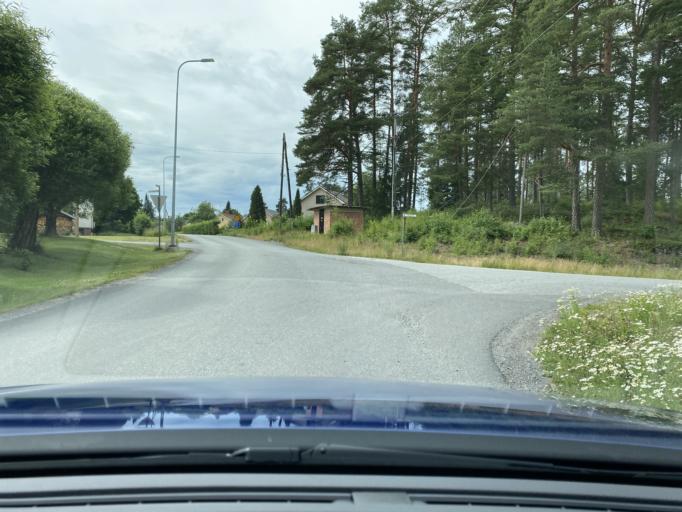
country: FI
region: Satakunta
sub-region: Rauma
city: Eura
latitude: 61.1087
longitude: 22.1446
